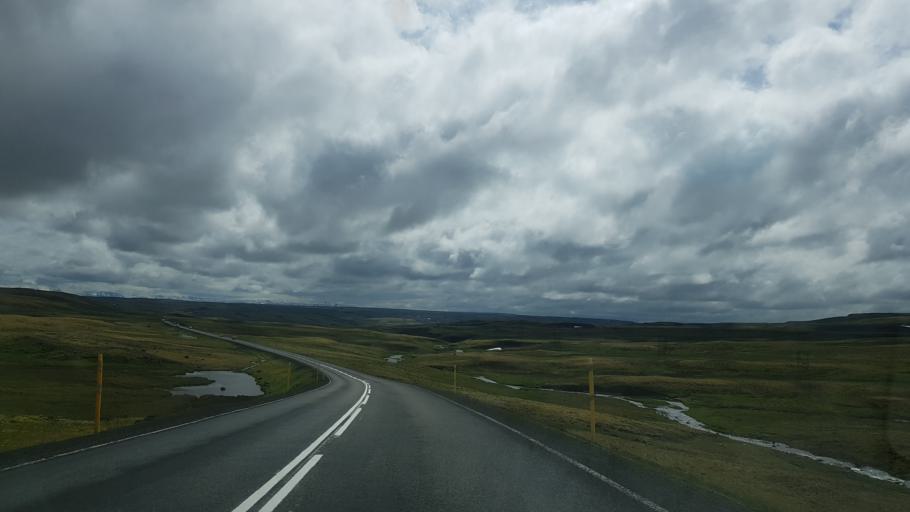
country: IS
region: West
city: Borgarnes
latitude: 64.9716
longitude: -21.0677
